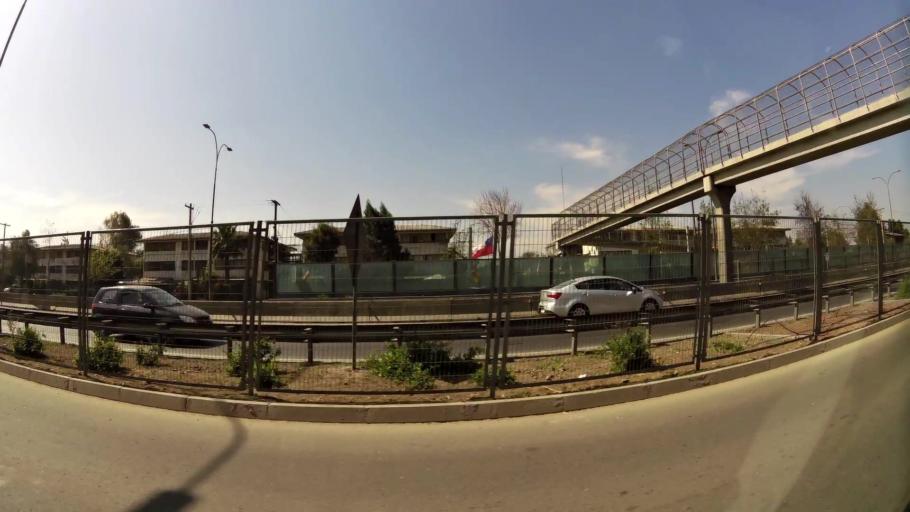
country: CL
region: Santiago Metropolitan
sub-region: Provincia de Santiago
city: Lo Prado
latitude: -33.3927
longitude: -70.7009
